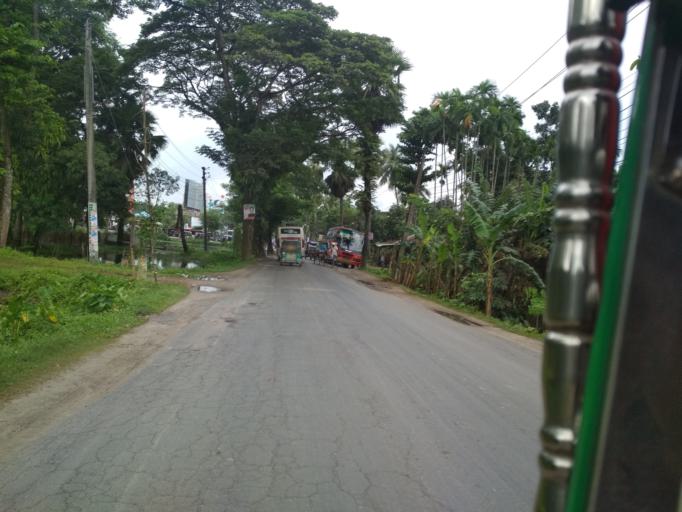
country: BD
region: Chittagong
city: Lakshmipur
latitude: 22.9462
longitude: 90.8150
